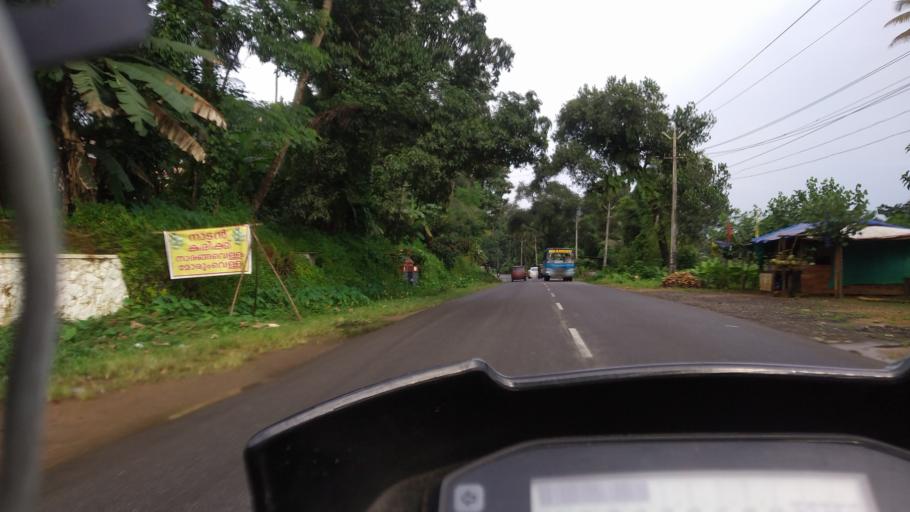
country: IN
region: Kerala
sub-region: Ernakulam
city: Kotamangalam
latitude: 10.0590
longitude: 76.6904
